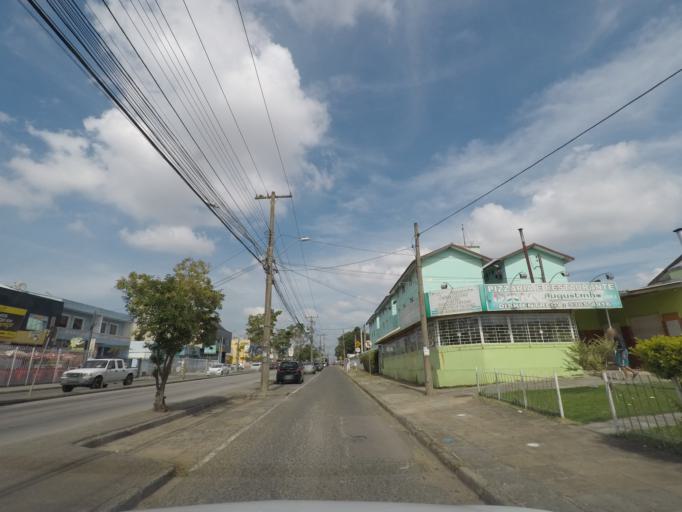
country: BR
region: Parana
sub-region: Pinhais
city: Pinhais
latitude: -25.4590
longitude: -49.2124
